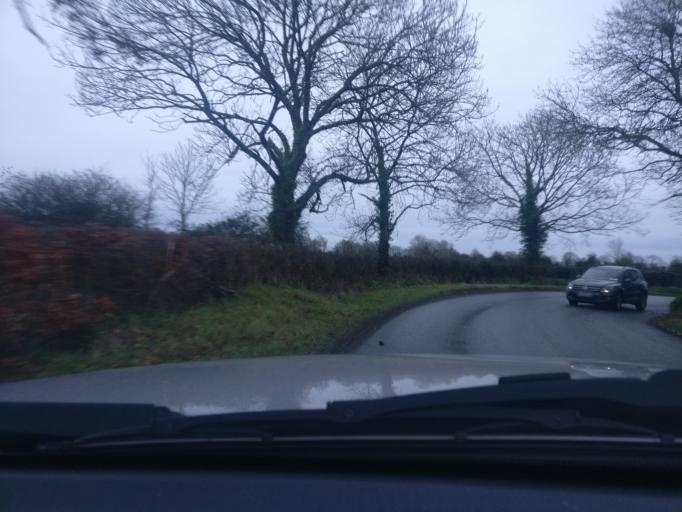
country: IE
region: Leinster
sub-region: Kildare
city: Maynooth
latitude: 53.4160
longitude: -6.6098
